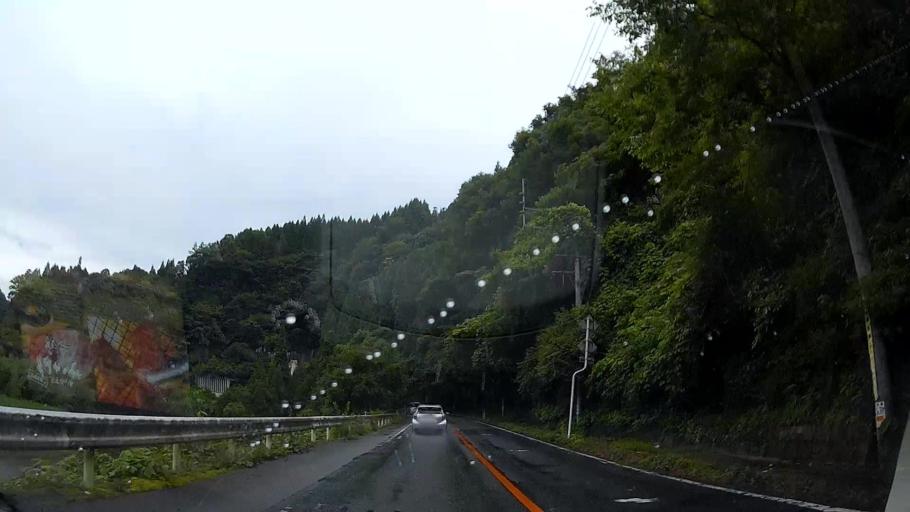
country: JP
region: Oita
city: Tsukawaki
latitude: 33.1620
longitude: 131.0447
